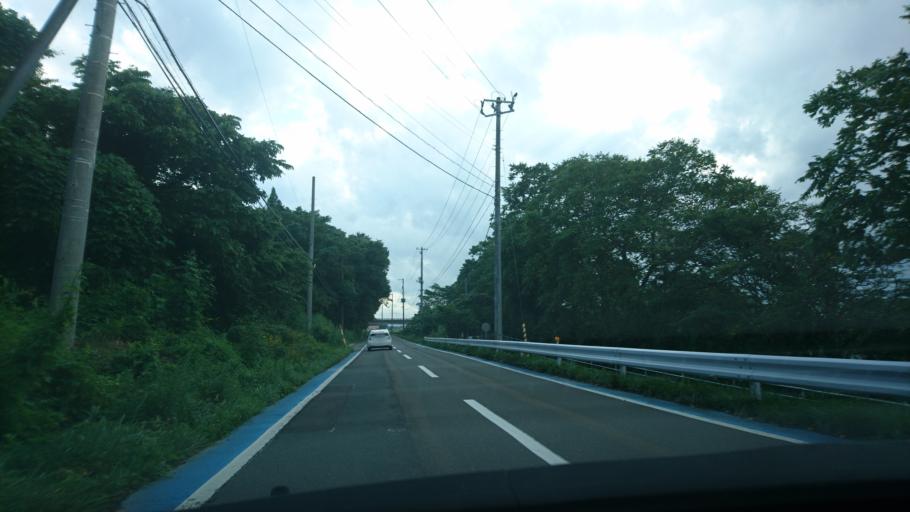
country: JP
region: Iwate
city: Kitakami
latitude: 39.2918
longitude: 141.1438
